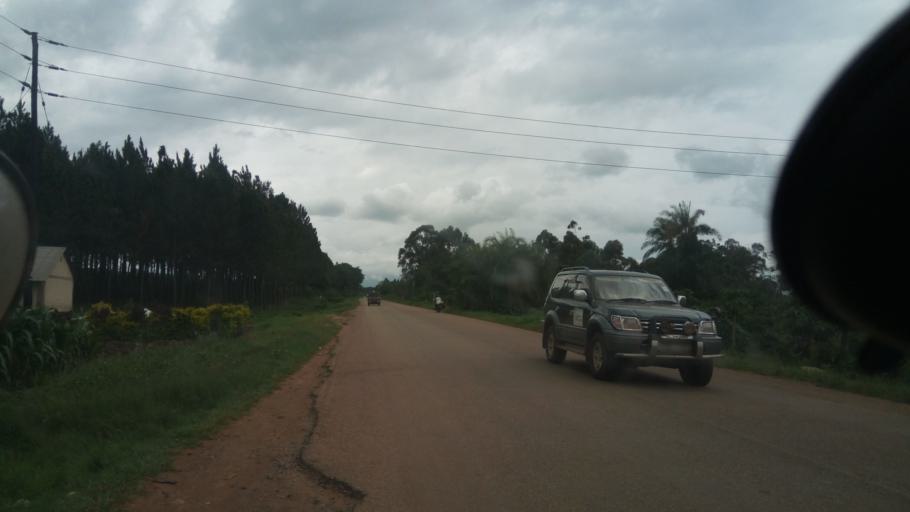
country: UG
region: Central Region
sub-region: Nakaseke District
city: Namasuba
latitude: 0.5577
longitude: 32.2214
